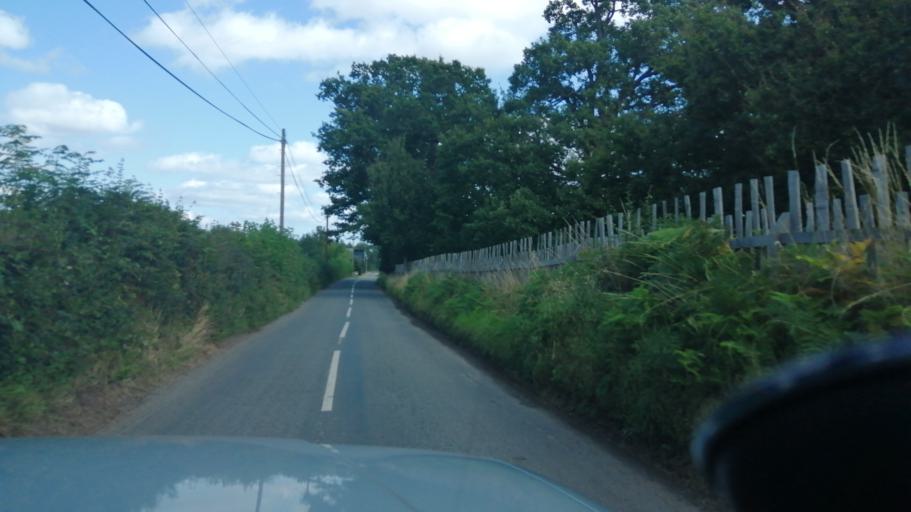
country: GB
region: England
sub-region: Herefordshire
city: Moccas
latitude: 52.0829
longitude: -2.9601
